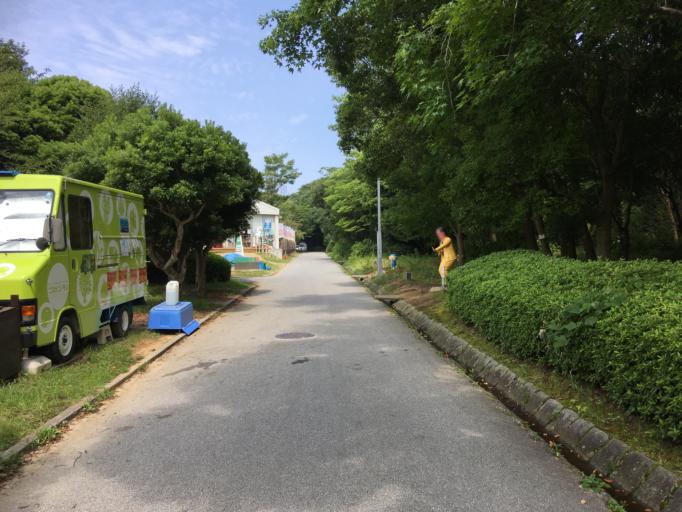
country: JP
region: Hyogo
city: Akashi
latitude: 34.5736
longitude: 135.0043
